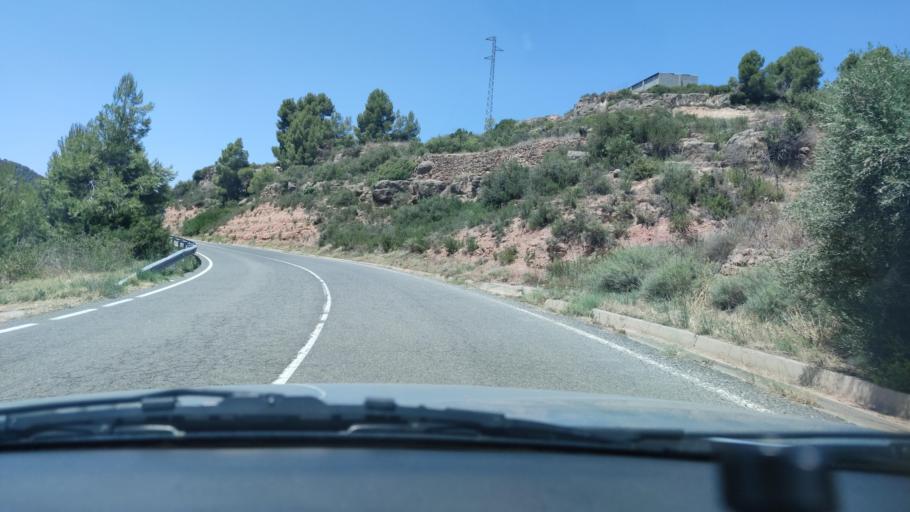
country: ES
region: Catalonia
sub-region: Provincia de Lleida
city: Juncosa
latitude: 41.3962
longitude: 0.7245
